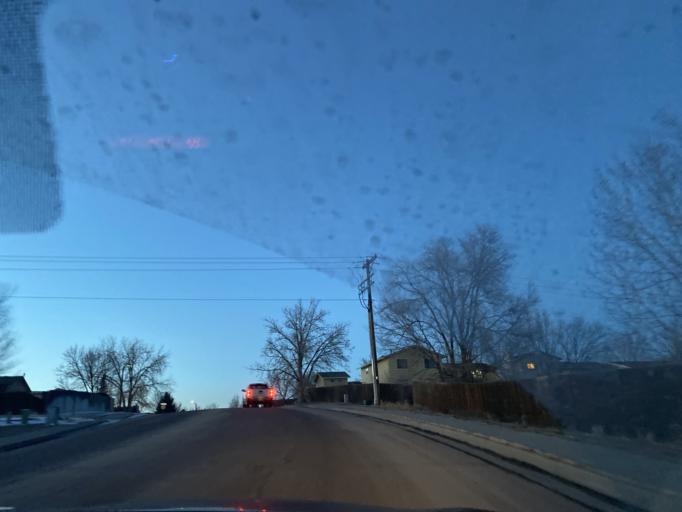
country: US
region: Colorado
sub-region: El Paso County
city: Security-Widefield
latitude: 38.7223
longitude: -104.6895
